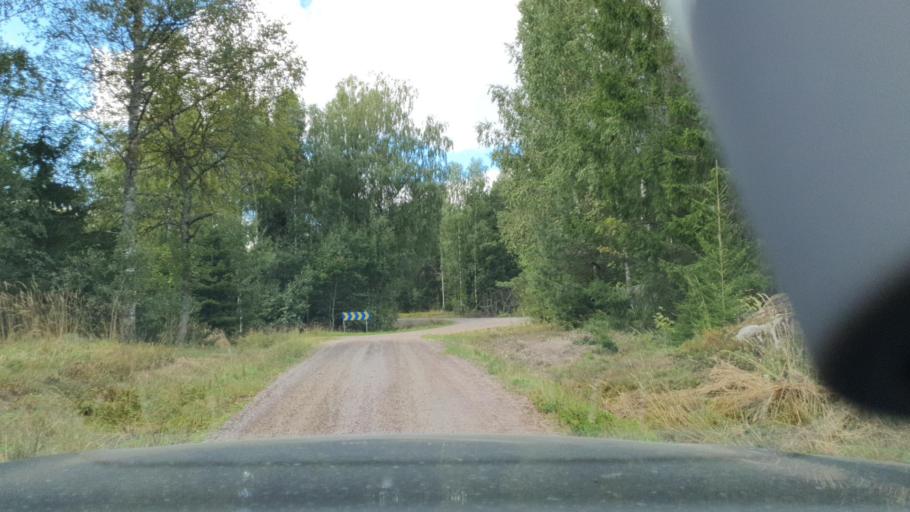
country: SE
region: Vaermland
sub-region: Storfors Kommun
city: Storfors
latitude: 59.5390
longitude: 14.0758
